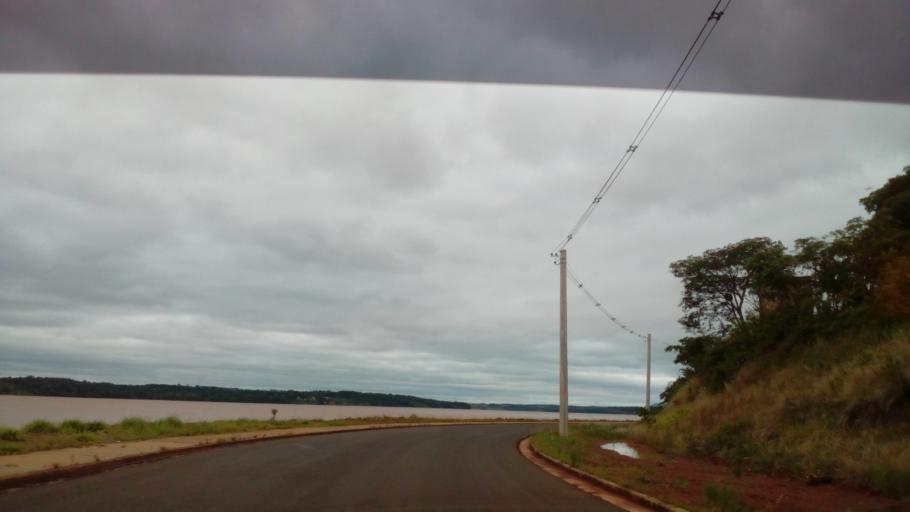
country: AR
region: Misiones
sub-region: Departamento de Candelaria
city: Candelaria
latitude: -27.4497
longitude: -55.7764
